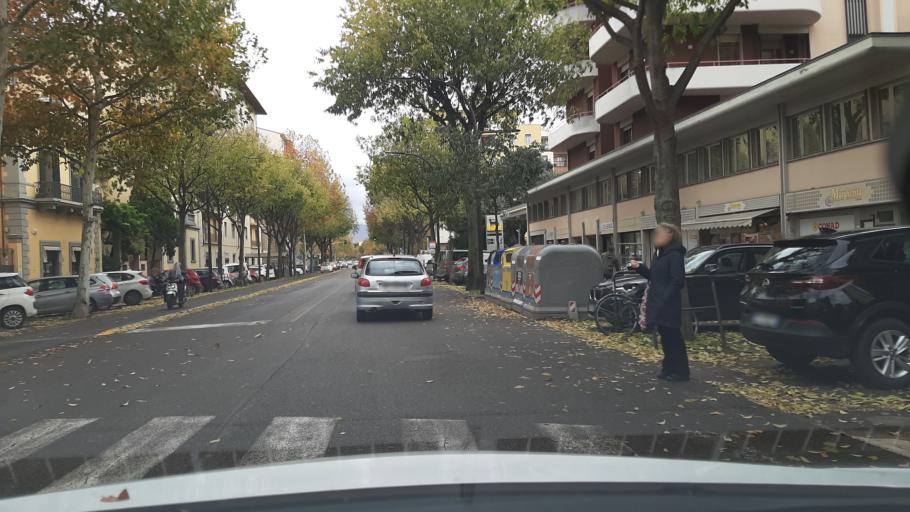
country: IT
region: Tuscany
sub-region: Province of Florence
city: Fiesole
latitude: 43.7810
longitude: 11.2787
